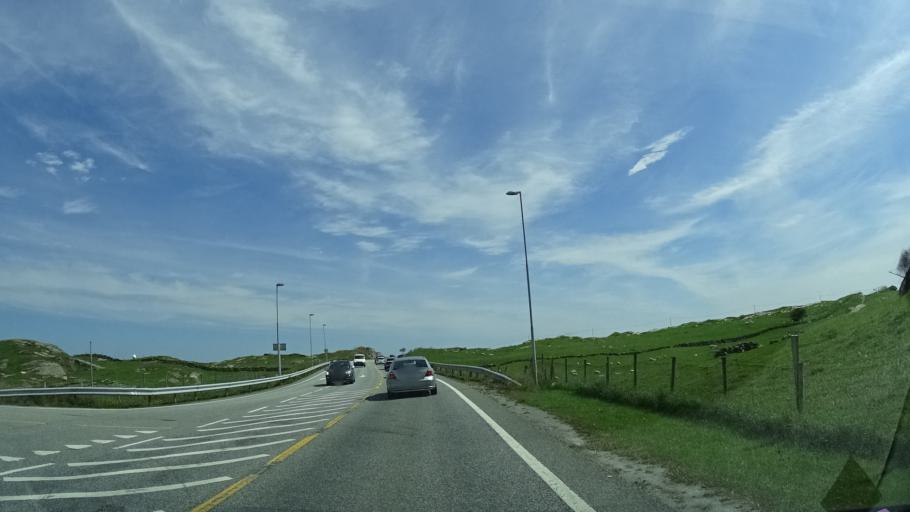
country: NO
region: Rogaland
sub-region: Rennesoy
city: Vikevag
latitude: 59.1376
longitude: 5.5945
